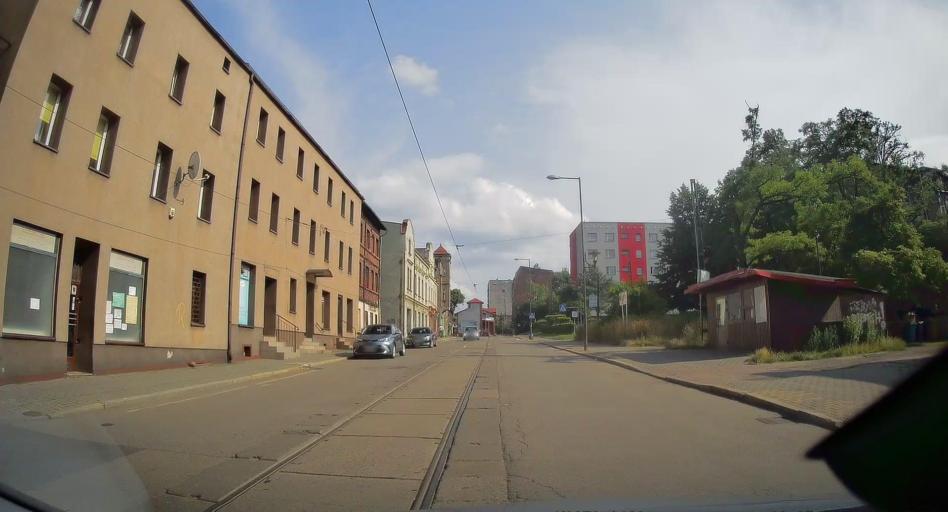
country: PL
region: Silesian Voivodeship
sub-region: Swietochlowice
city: Swietochlowice
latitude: 50.3136
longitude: 18.9136
